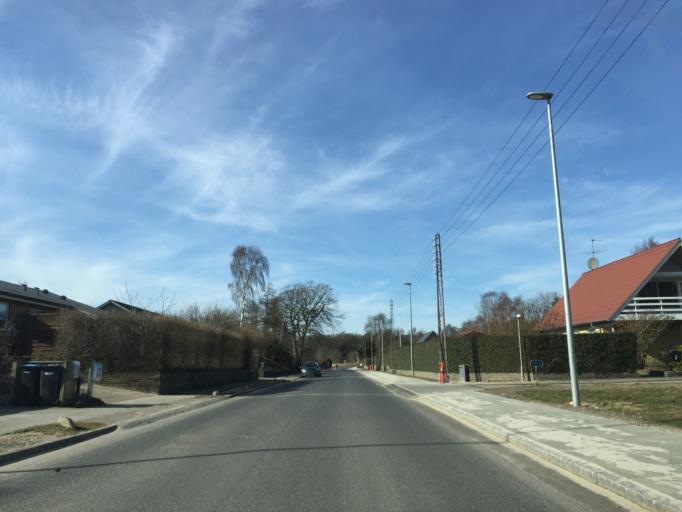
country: DK
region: Central Jutland
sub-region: Silkeborg Kommune
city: Silkeborg
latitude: 56.1937
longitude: 9.5355
